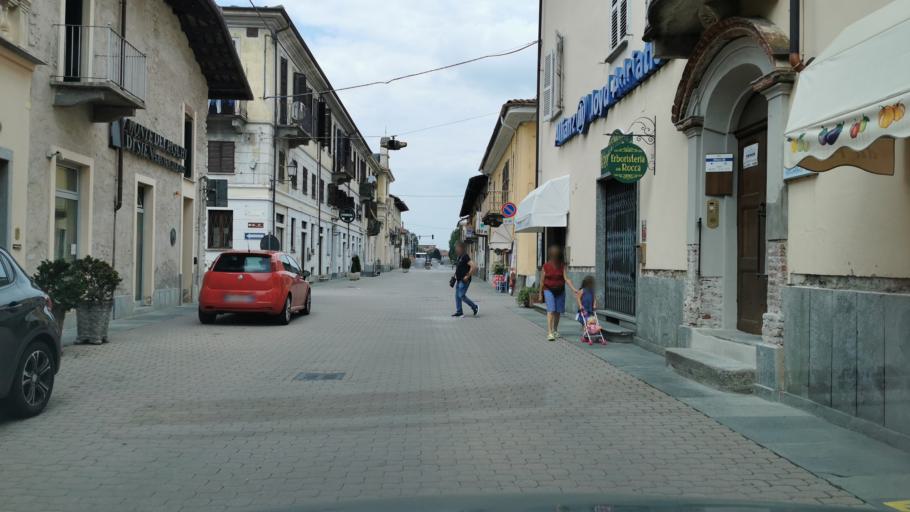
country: IT
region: Piedmont
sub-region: Provincia di Torino
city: Cavour
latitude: 44.7854
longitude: 7.3749
